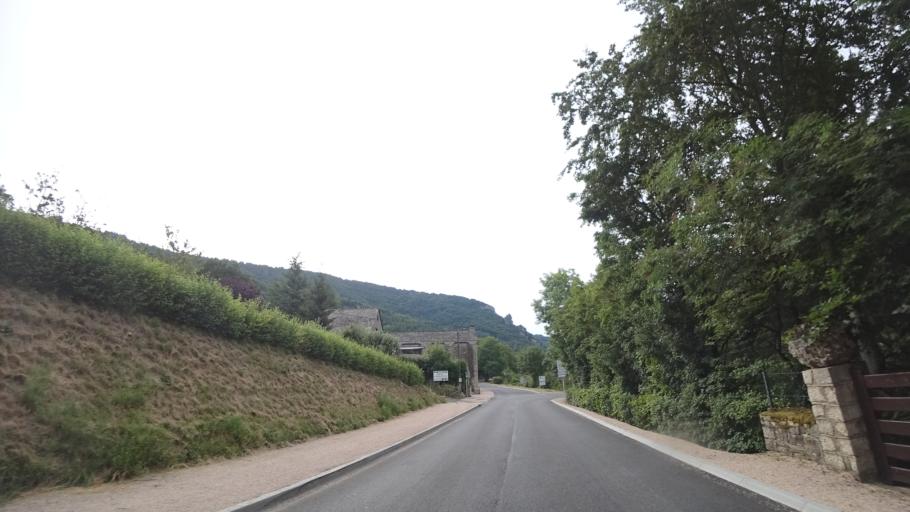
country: FR
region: Languedoc-Roussillon
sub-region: Departement de la Lozere
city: La Canourgue
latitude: 44.4176
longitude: 3.2310
